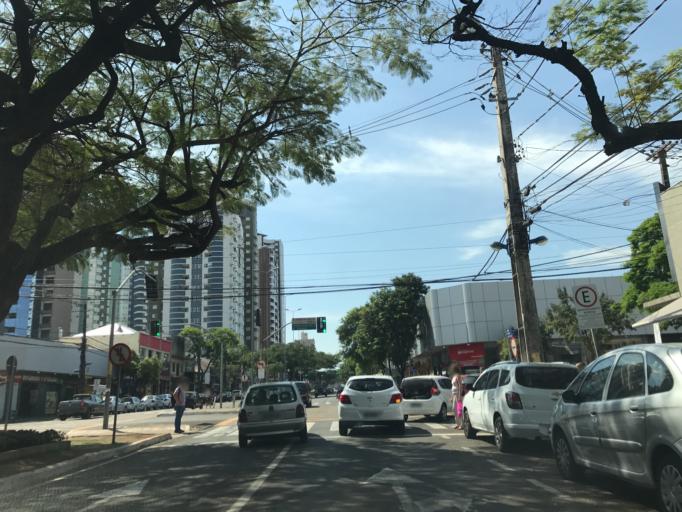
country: BR
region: Parana
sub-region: Maringa
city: Maringa
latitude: -23.4203
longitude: -51.9330
